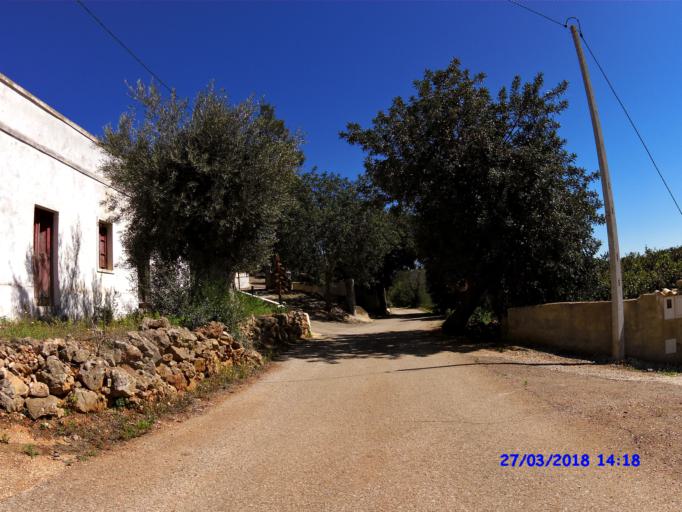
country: PT
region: Faro
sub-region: Loule
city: Boliqueime
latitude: 37.2075
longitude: -8.1675
